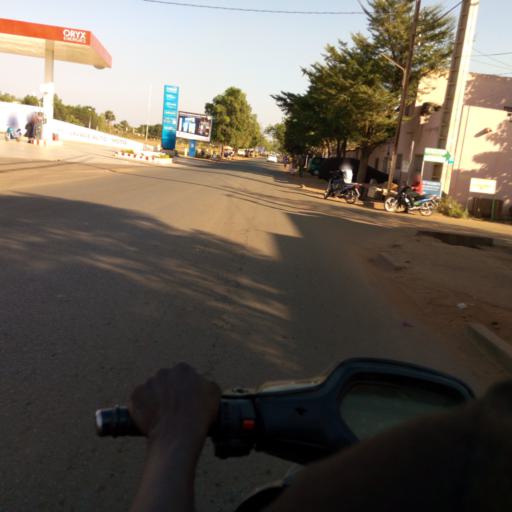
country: ML
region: Bamako
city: Bamako
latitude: 12.6524
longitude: -8.0169
